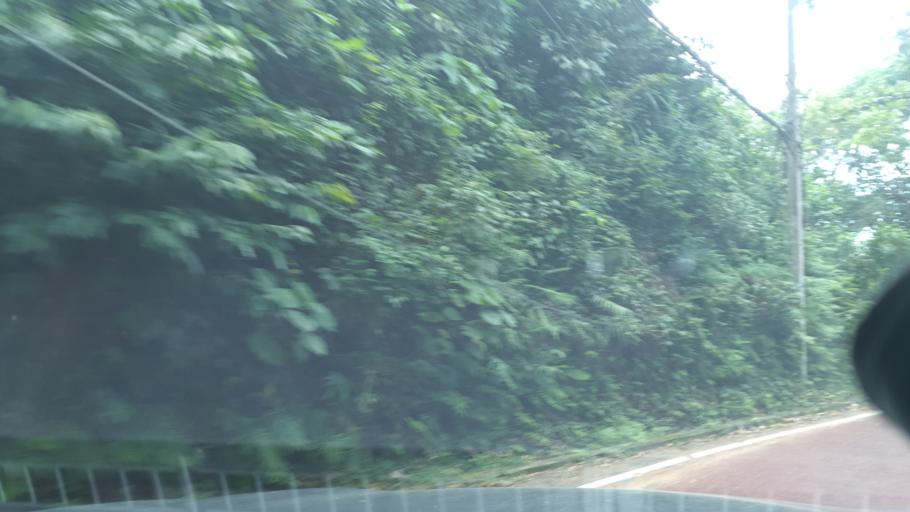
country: TH
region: Phuket
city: Thalang
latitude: 8.0423
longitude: 98.2778
